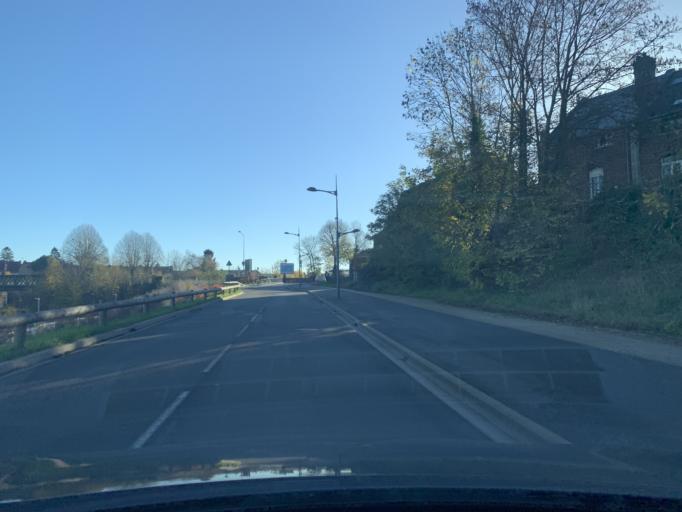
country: FR
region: Nord-Pas-de-Calais
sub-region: Departement du Nord
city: Cambrai
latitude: 50.1738
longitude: 3.2447
